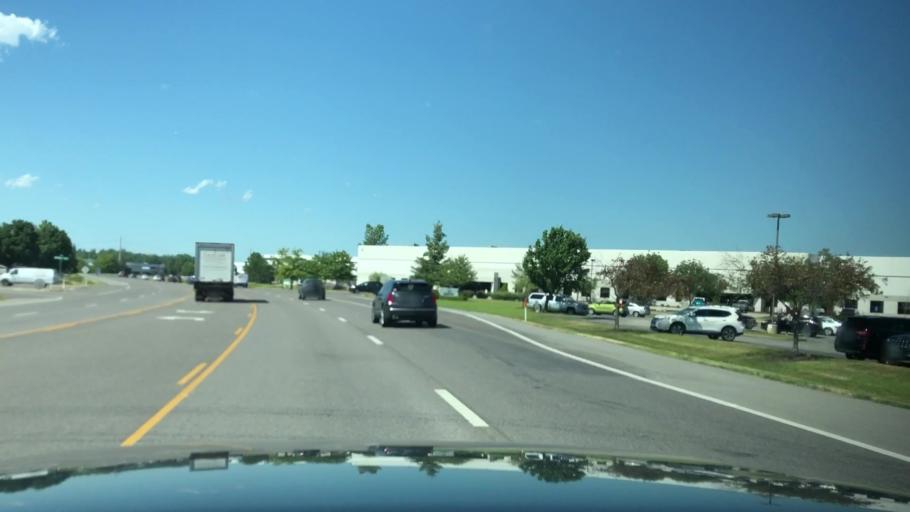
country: US
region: Missouri
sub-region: Saint Charles County
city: Saint Charles
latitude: 38.7810
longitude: -90.4590
